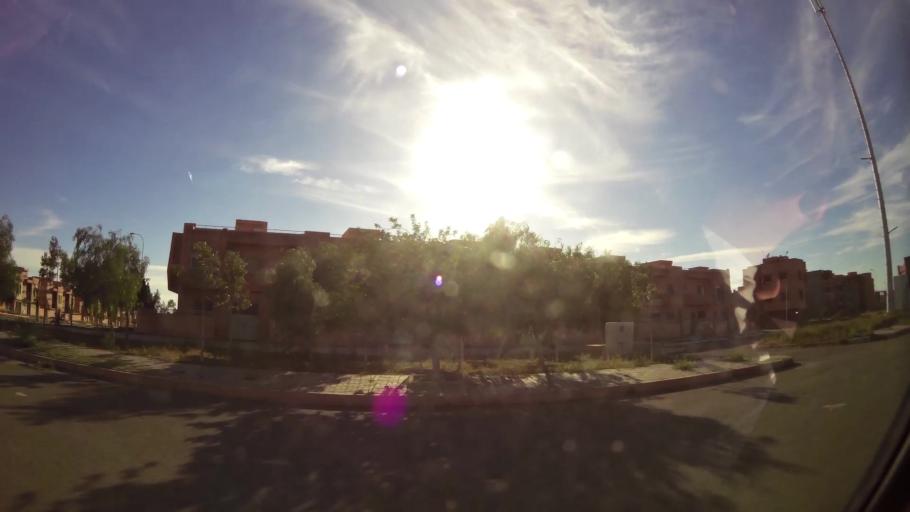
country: MA
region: Marrakech-Tensift-Al Haouz
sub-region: Marrakech
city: Marrakesh
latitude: 31.7519
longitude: -8.1001
